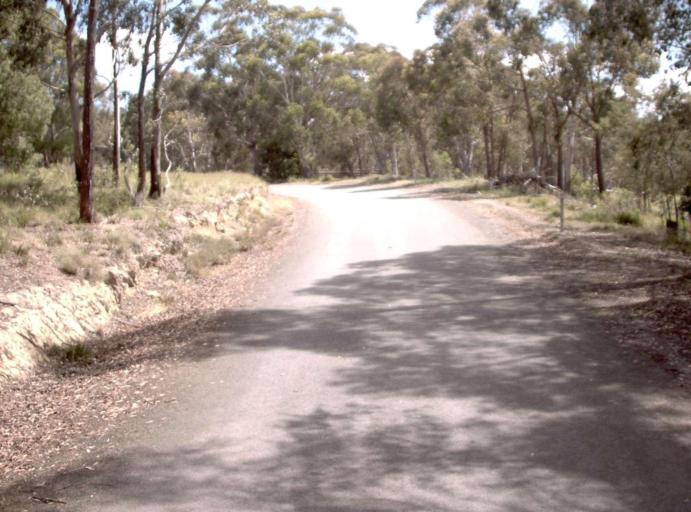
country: AU
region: New South Wales
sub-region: Bombala
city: Bombala
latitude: -37.1769
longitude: 148.6975
